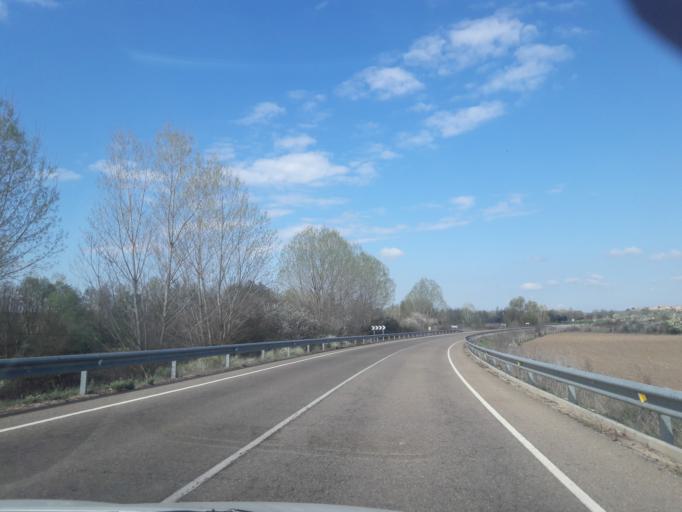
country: ES
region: Castille and Leon
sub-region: Provincia de Salamanca
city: Ciudad Rodrigo
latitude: 40.5750
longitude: -6.4971
